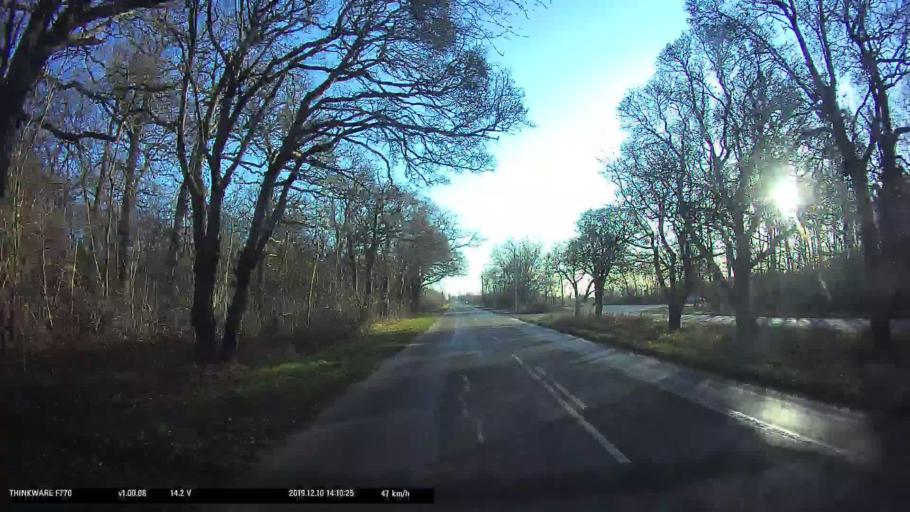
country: DK
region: Capital Region
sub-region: Tarnby Kommune
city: Tarnby
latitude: 55.5729
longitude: 12.5808
